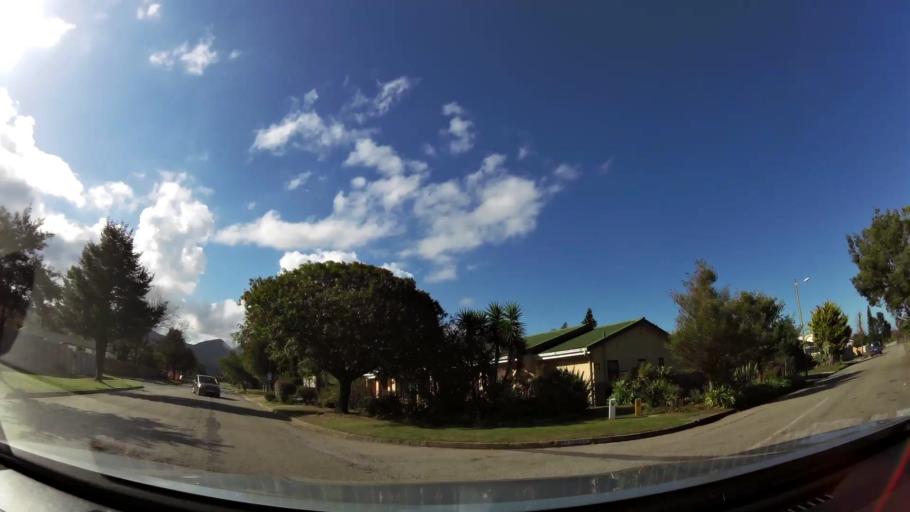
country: ZA
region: Western Cape
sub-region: Eden District Municipality
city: George
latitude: -33.9660
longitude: 22.4860
